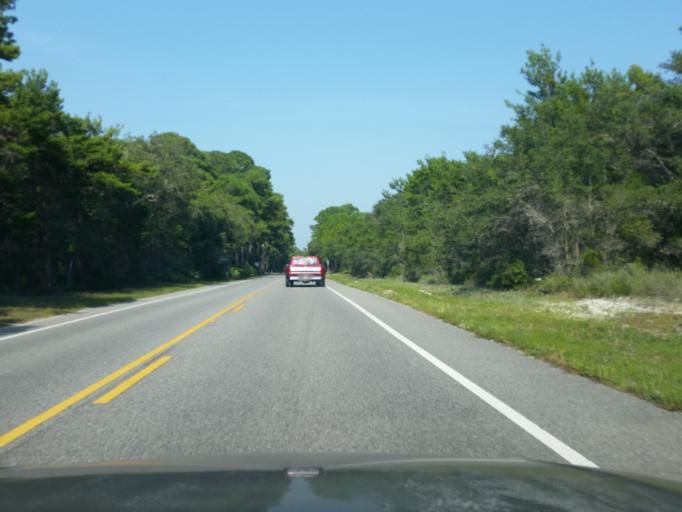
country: US
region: Alabama
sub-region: Baldwin County
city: Gulf Shores
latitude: 30.2517
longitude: -87.8125
